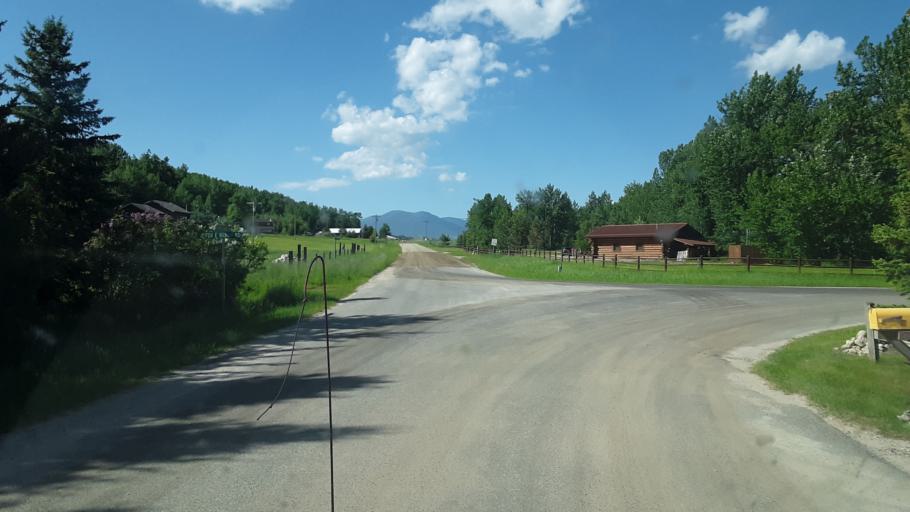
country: US
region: Montana
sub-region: Carbon County
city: Red Lodge
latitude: 45.2774
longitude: -109.2083
